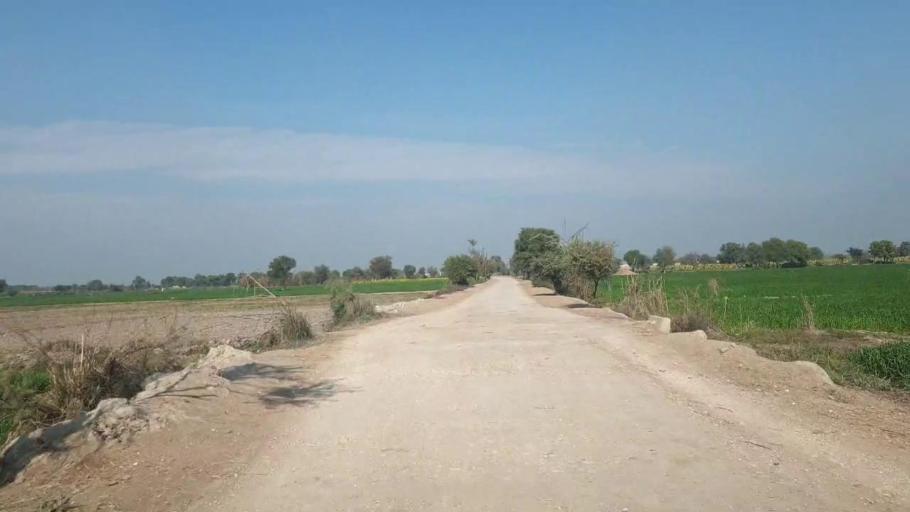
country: PK
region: Sindh
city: Shahdadpur
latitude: 25.9777
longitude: 68.5292
